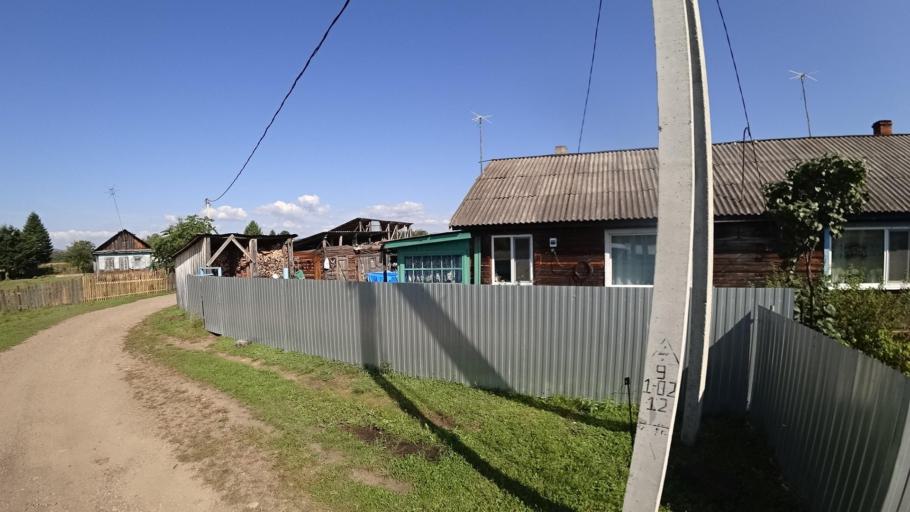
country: RU
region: Jewish Autonomous Oblast
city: Bira
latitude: 48.9931
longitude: 132.4553
